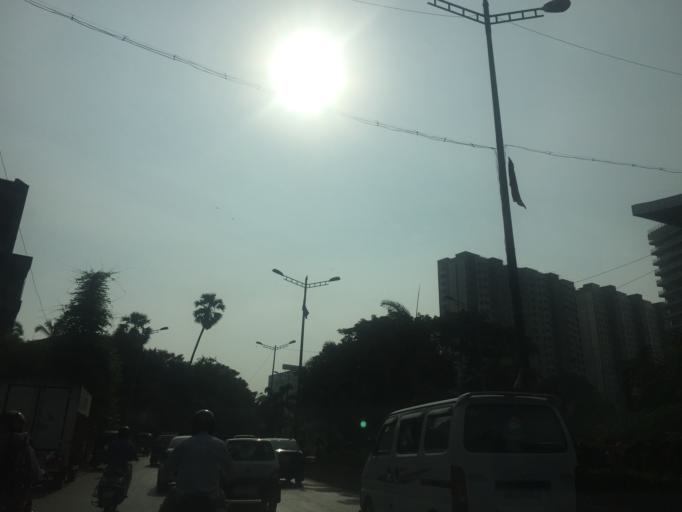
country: IN
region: Maharashtra
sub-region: Mumbai Suburban
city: Powai
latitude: 19.1260
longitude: 72.8943
